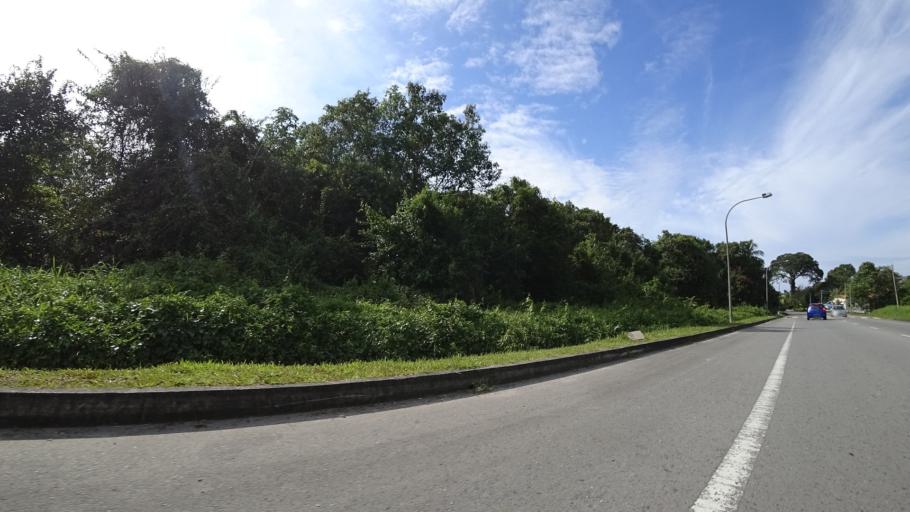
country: BN
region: Brunei and Muara
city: Bandar Seri Begawan
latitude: 4.8711
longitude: 114.8079
